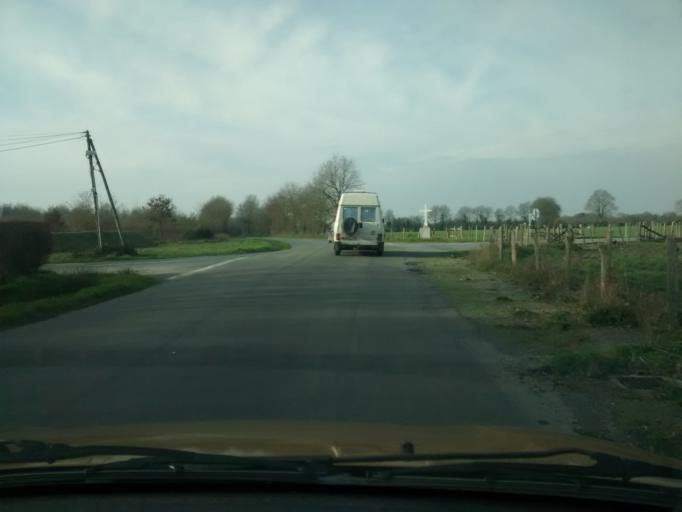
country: FR
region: Pays de la Loire
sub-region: Departement de la Loire-Atlantique
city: Heric
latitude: 47.4060
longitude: -1.6774
